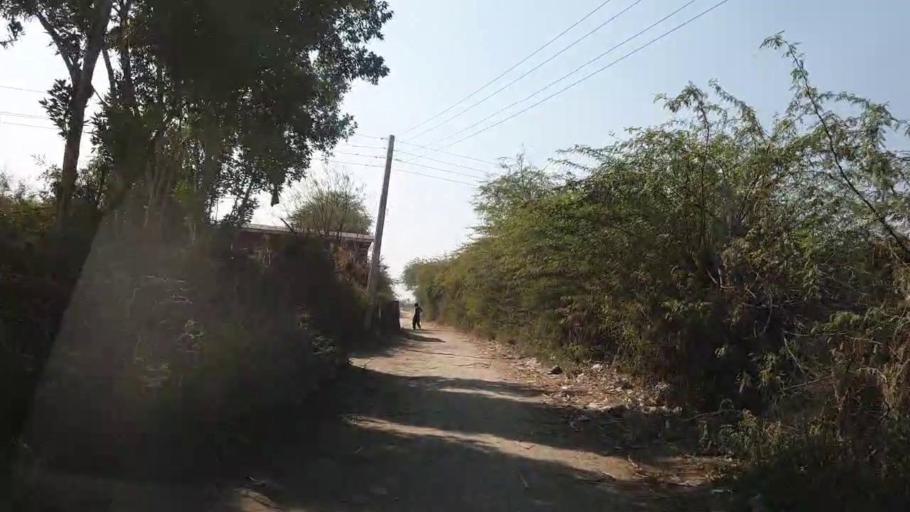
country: PK
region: Sindh
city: Matiari
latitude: 25.5156
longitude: 68.4603
